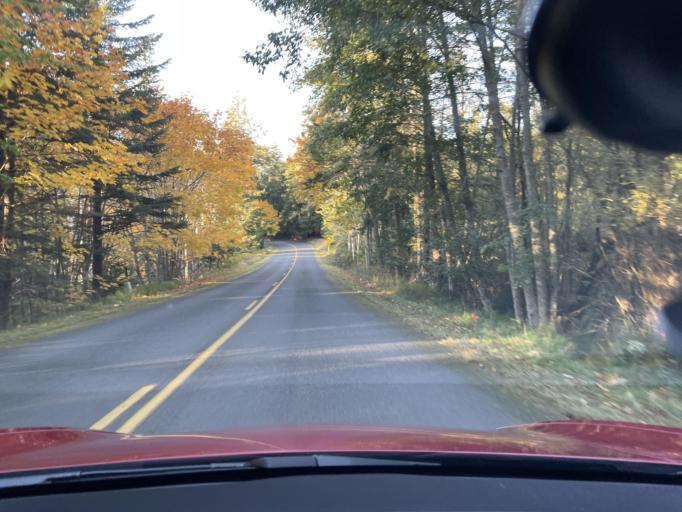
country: US
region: Washington
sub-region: San Juan County
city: Friday Harbor
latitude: 48.5484
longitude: -123.1589
